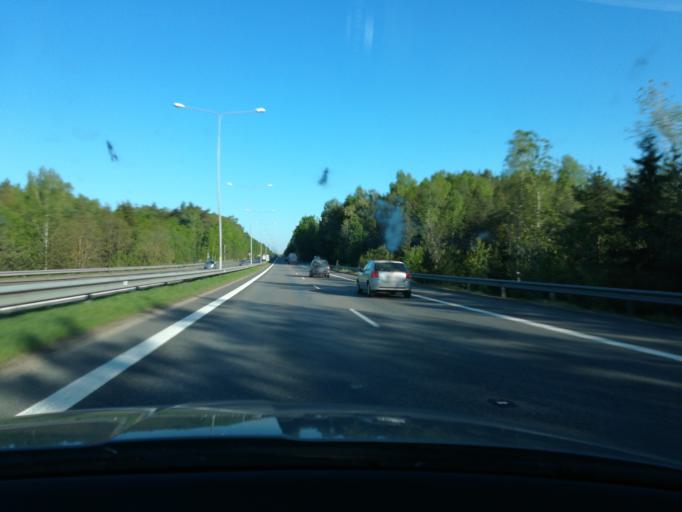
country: LT
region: Kauno apskritis
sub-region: Kauno rajonas
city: Karmelava
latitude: 54.9028
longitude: 24.1295
